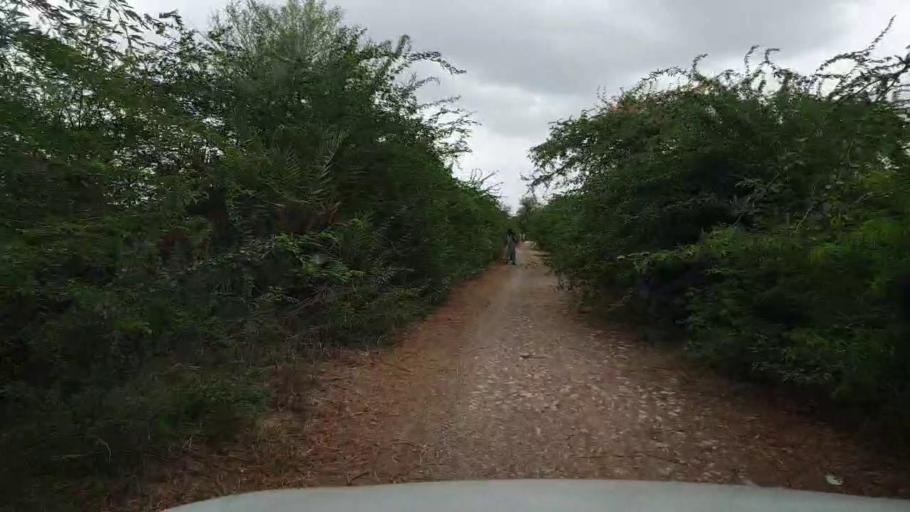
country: PK
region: Sindh
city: Kario
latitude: 24.7481
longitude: 68.4847
